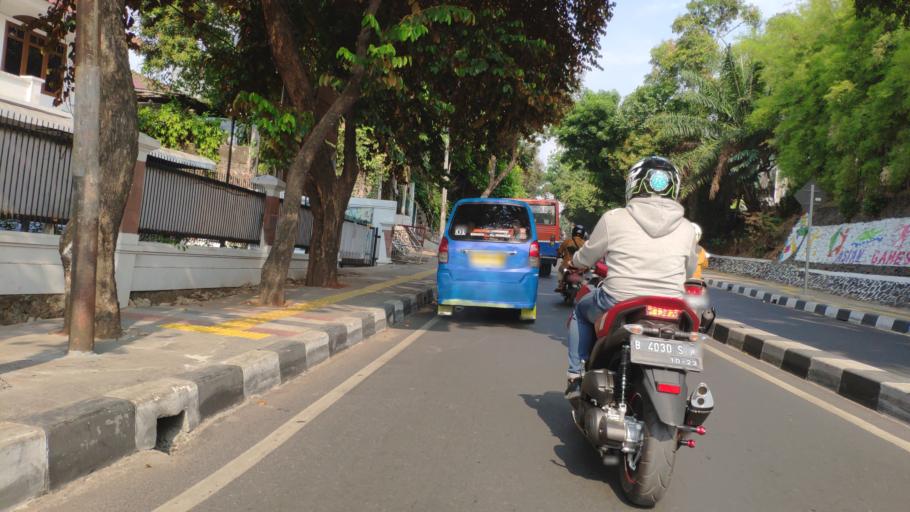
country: ID
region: Jakarta Raya
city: Jakarta
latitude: -6.2861
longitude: 106.8280
